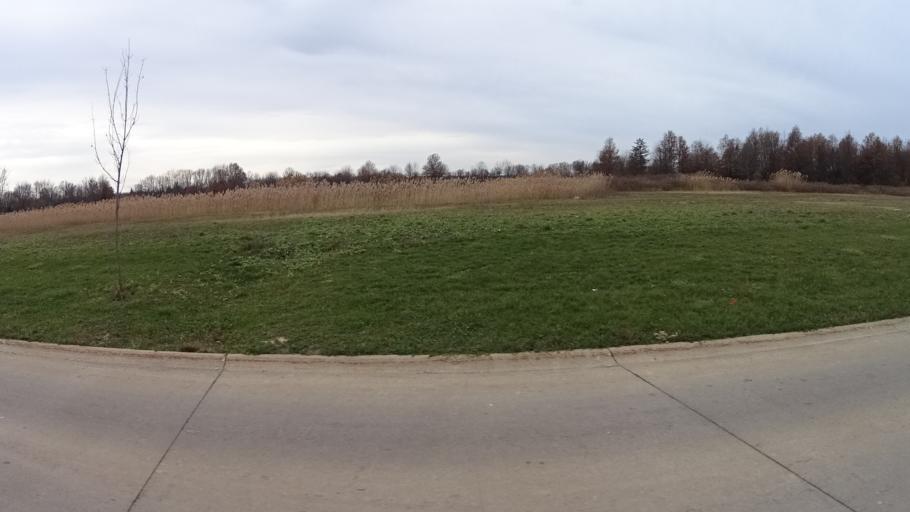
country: US
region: Ohio
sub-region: Lorain County
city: North Ridgeville
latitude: 41.3869
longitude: -82.0437
